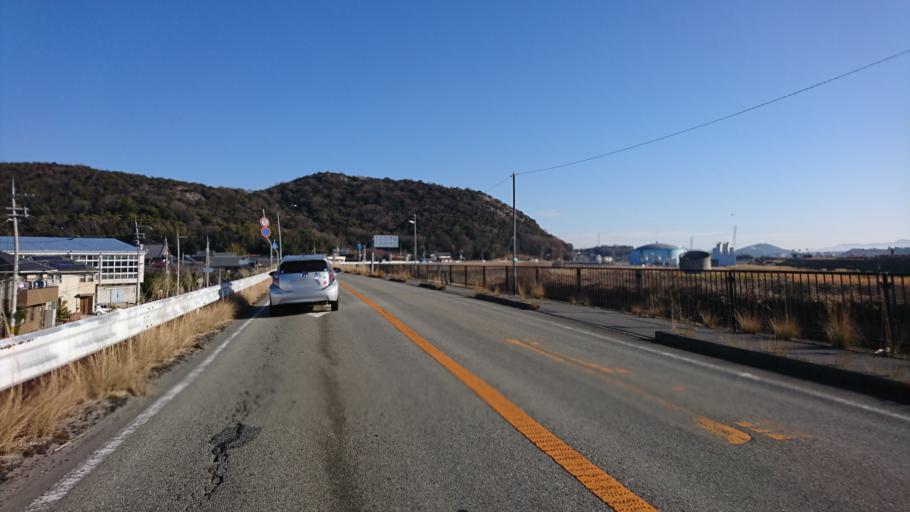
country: JP
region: Hyogo
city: Kakogawacho-honmachi
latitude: 34.7837
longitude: 134.8458
